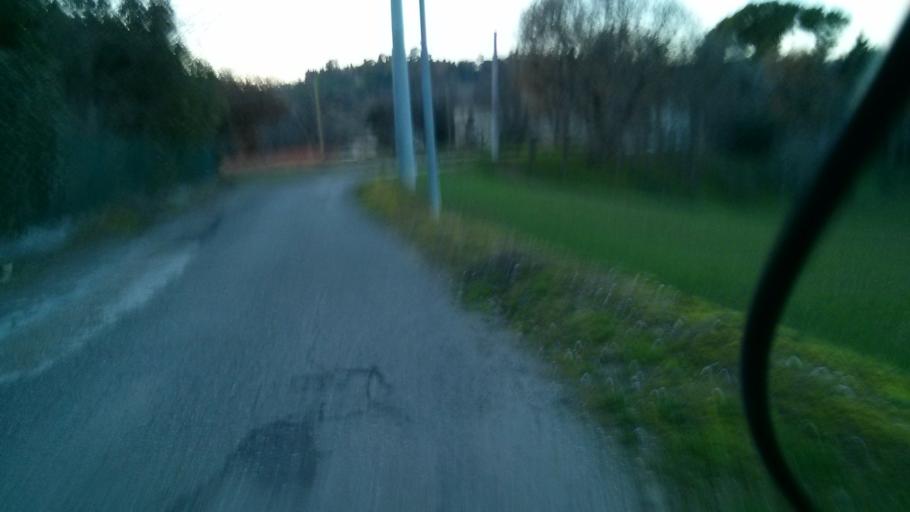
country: IT
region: The Marches
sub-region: Provincia di Pesaro e Urbino
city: Fano
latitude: 43.8490
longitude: 13.0016
